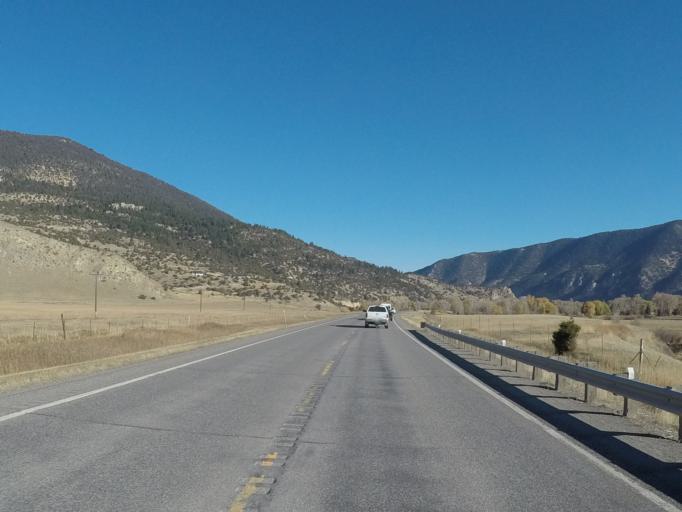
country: US
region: Montana
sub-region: Park County
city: Livingston
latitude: 45.5704
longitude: -110.5893
